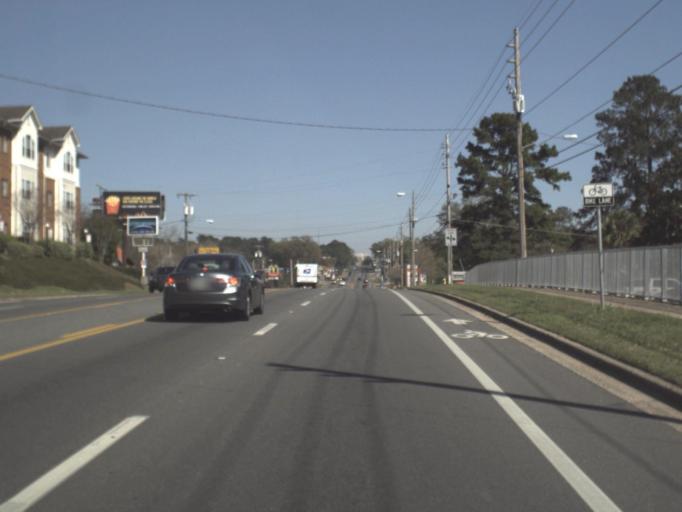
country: US
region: Florida
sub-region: Leon County
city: Tallahassee
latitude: 30.4408
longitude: -84.3224
